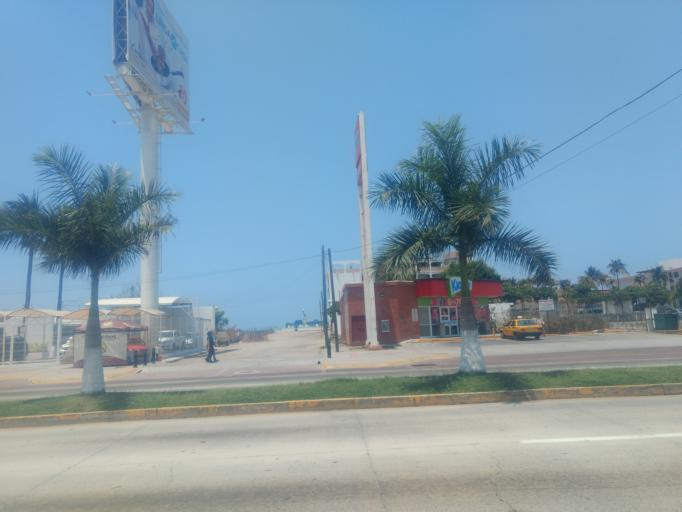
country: MX
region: Colima
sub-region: Manzanillo
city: Manzanillo
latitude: 19.0988
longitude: -104.3232
